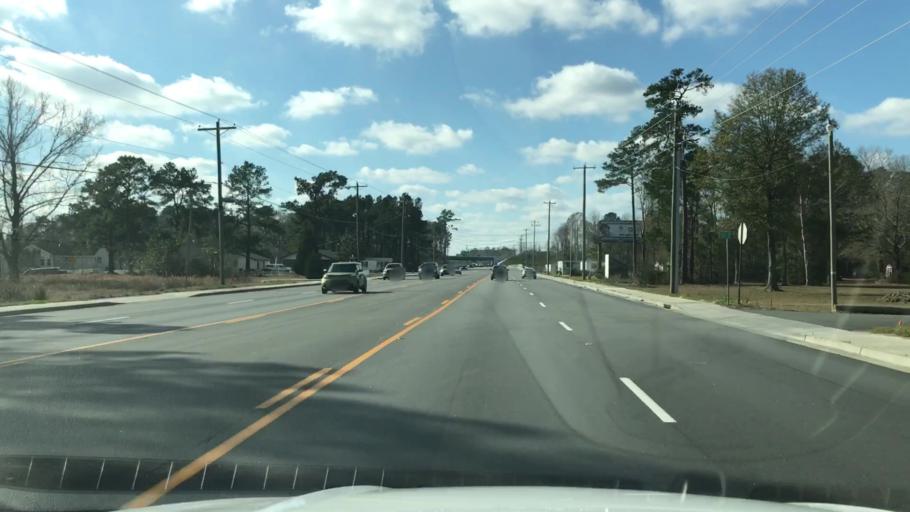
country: US
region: South Carolina
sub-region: Horry County
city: Socastee
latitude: 33.6585
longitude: -79.0145
